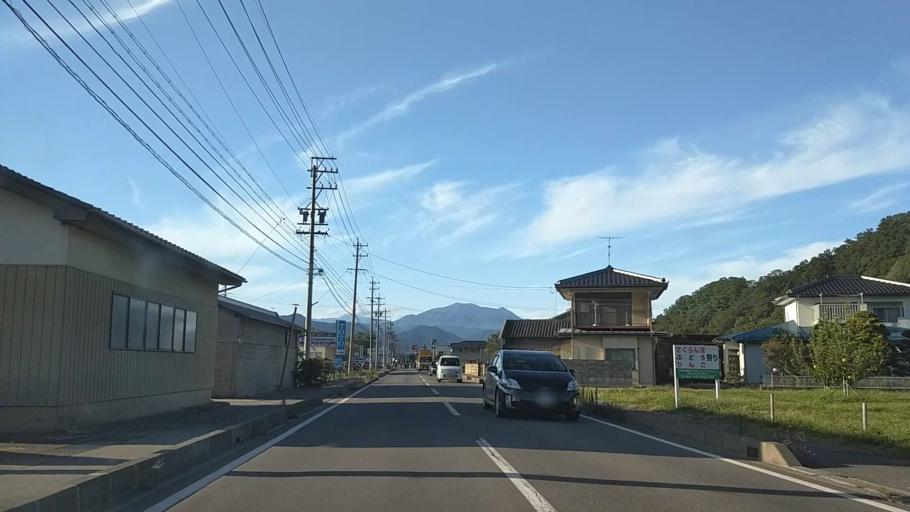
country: JP
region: Nagano
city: Nagano-shi
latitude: 36.5837
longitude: 138.2003
